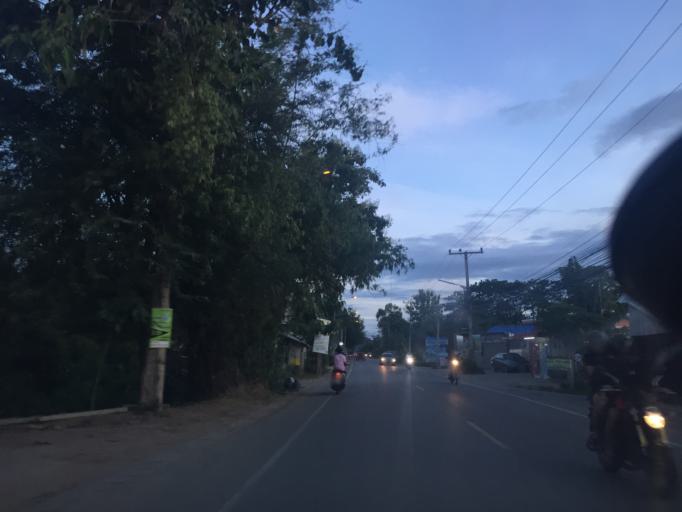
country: TH
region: Lamphun
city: Lamphun
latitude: 18.5525
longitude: 99.0355
